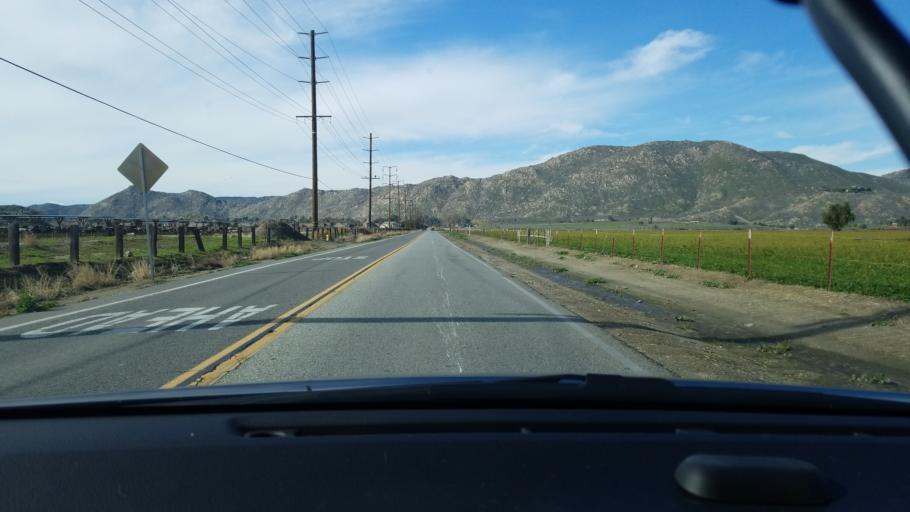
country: US
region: California
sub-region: Riverside County
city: Hemet
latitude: 33.7728
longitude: -117.0170
